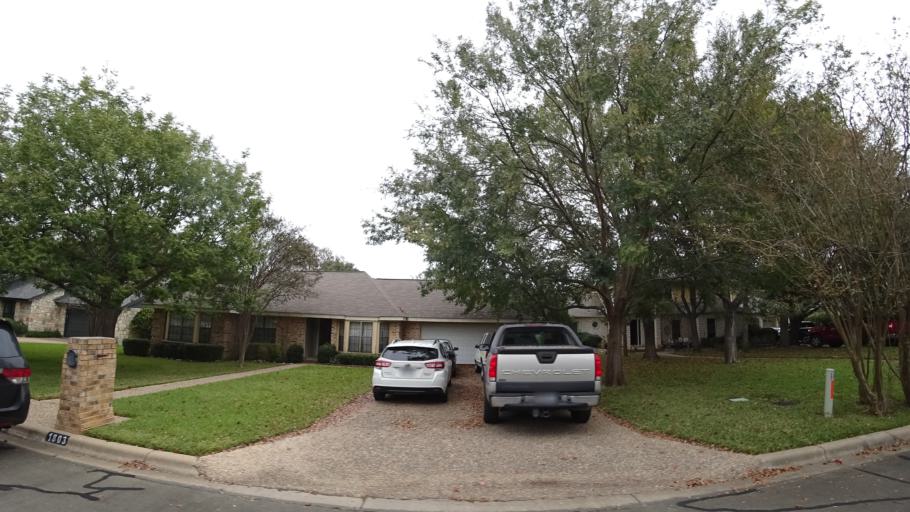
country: US
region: Texas
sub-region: Williamson County
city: Round Rock
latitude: 30.4929
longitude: -97.7040
